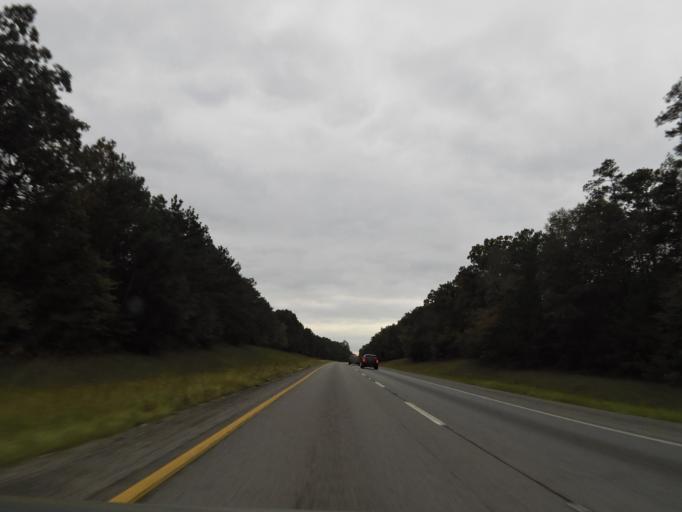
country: US
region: Alabama
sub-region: Saint Clair County
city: Steele
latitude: 33.8991
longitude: -86.2343
